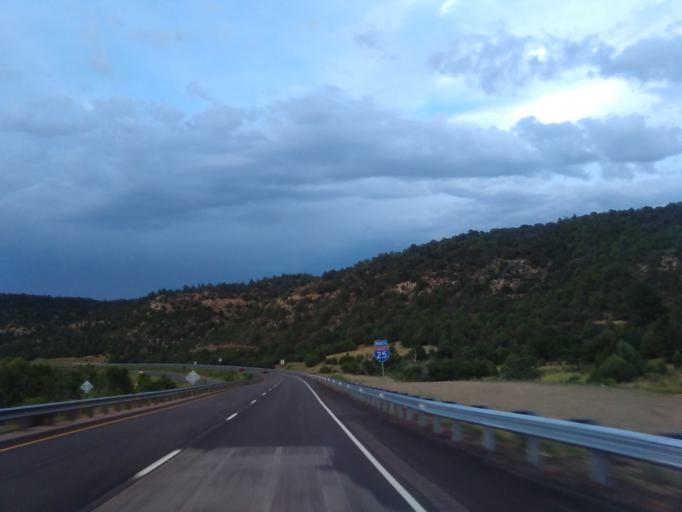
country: US
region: Colorado
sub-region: Las Animas County
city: Trinidad
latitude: 37.0901
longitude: -104.5212
